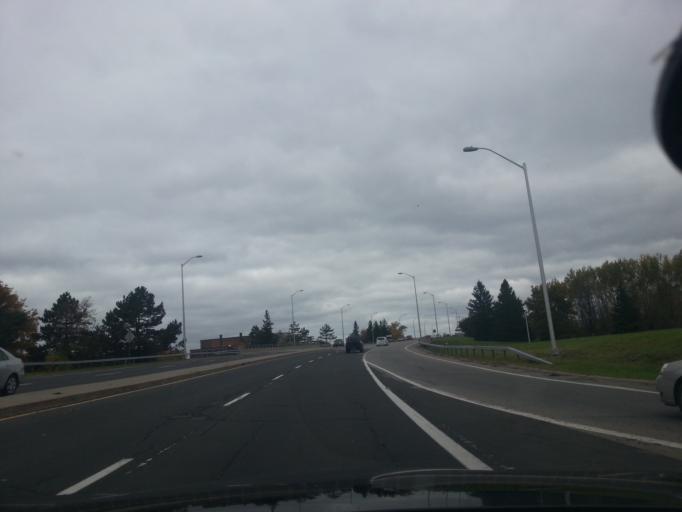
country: CA
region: Ontario
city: Ottawa
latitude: 45.3737
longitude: -75.6820
